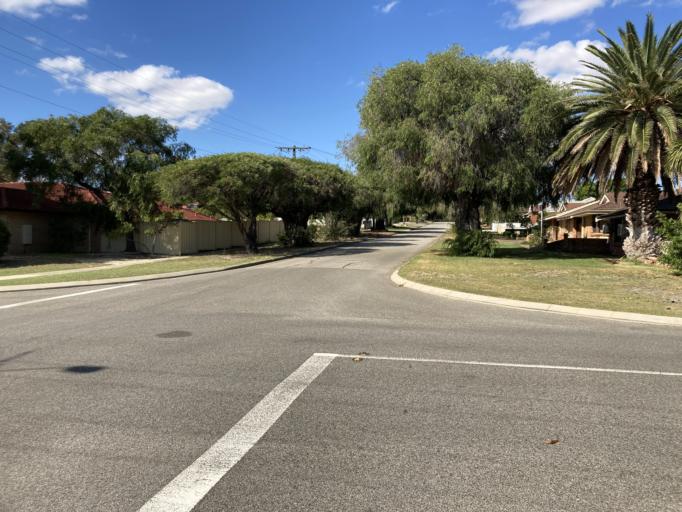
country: AU
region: Western Australia
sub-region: Melville
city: Palmyra
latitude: -32.0413
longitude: 115.7906
